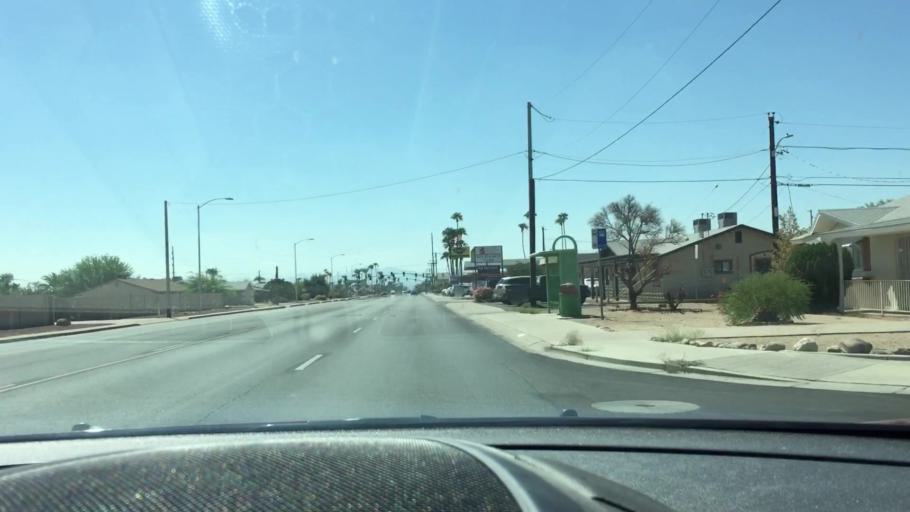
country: US
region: Arizona
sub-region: Maricopa County
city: Youngtown
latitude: 33.5973
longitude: -112.2988
